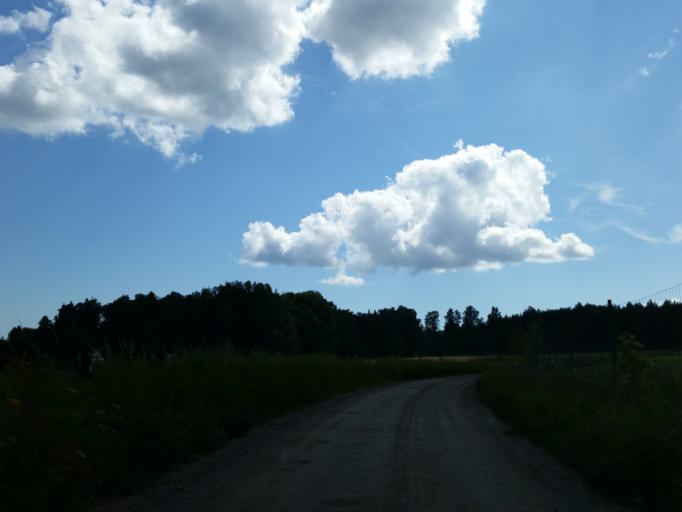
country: SE
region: Stockholm
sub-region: Sodertalje Kommun
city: Pershagen
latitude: 59.0650
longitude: 17.6615
